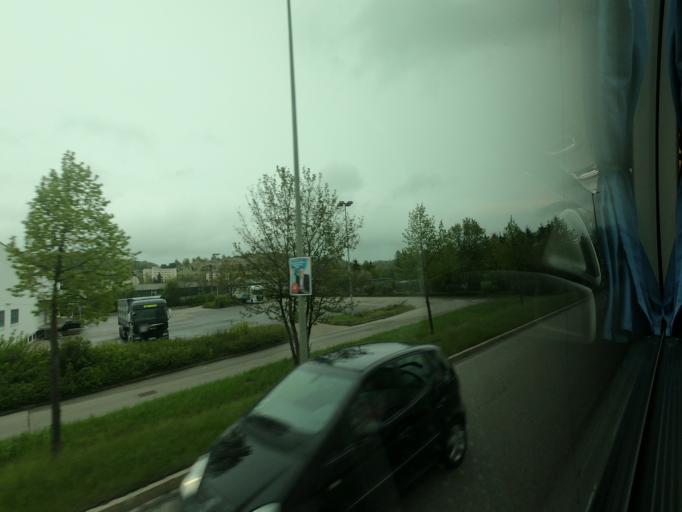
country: DE
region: Baden-Wuerttemberg
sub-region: Regierungsbezirk Stuttgart
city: Heidenheim an der Brenz
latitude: 48.7007
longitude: 10.1663
